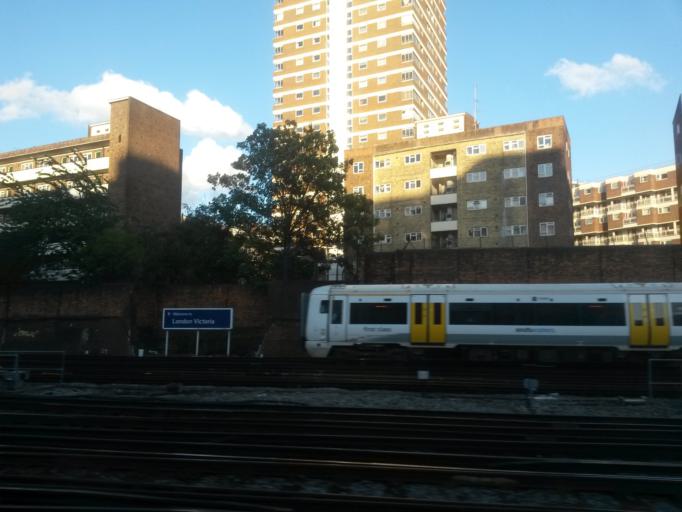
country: GB
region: England
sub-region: Greater London
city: Battersea
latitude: 51.4907
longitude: -0.1480
